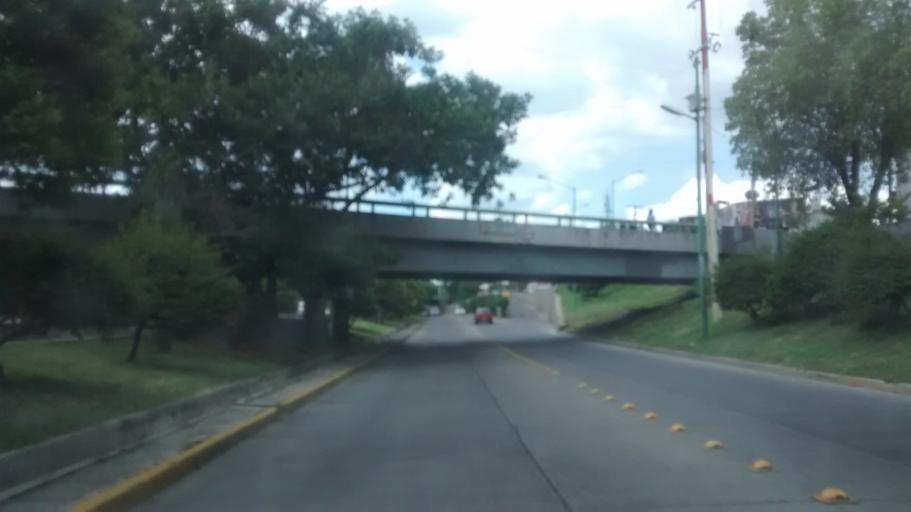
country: MX
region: Guanajuato
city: Leon
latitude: 21.1307
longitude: -101.6774
